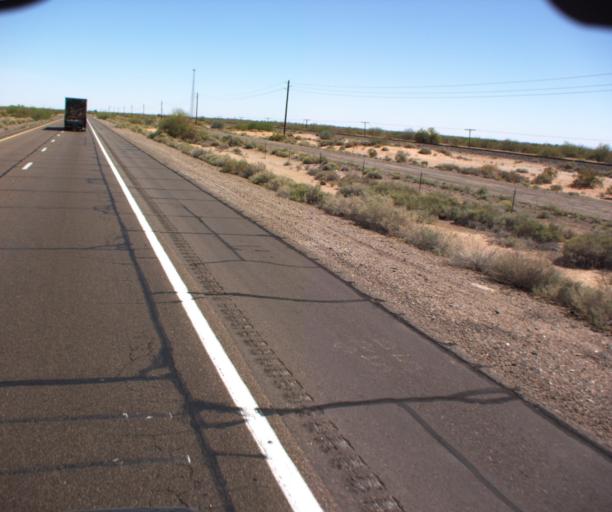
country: US
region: Arizona
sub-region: Maricopa County
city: Gila Bend
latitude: 32.8326
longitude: -113.3791
